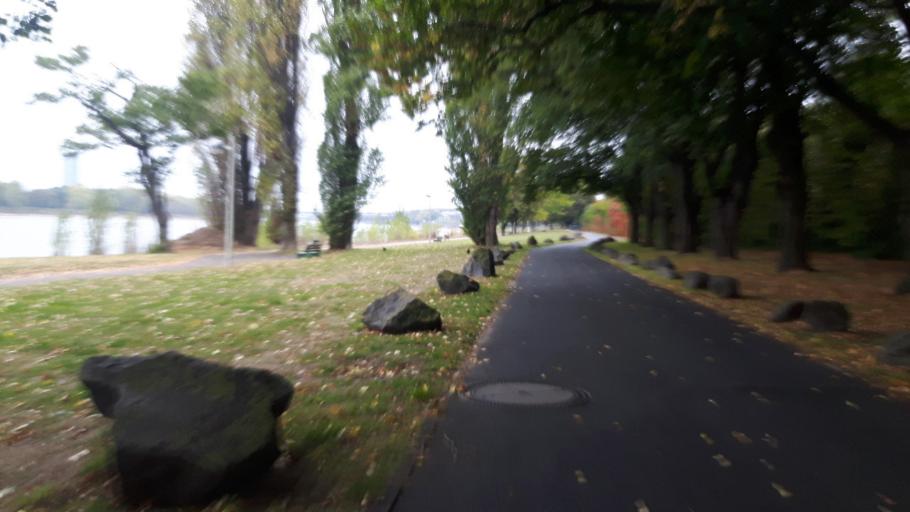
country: DE
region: North Rhine-Westphalia
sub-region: Regierungsbezirk Koln
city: Konigswinter
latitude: 50.7096
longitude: 7.1658
